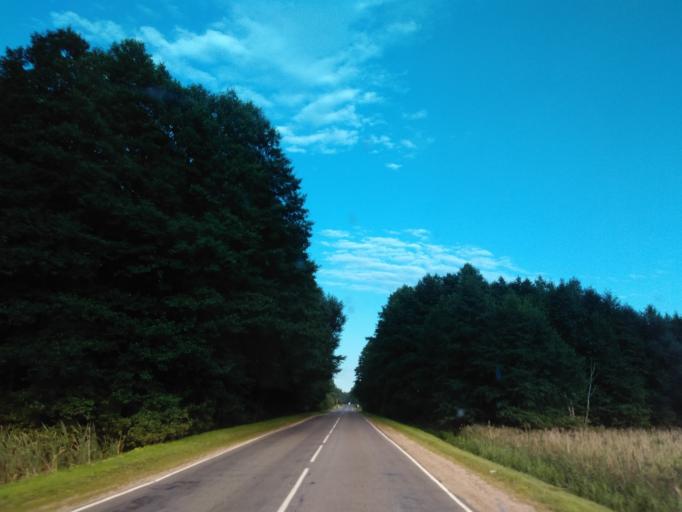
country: BY
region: Minsk
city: Uzda
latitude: 53.4211
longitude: 27.4009
